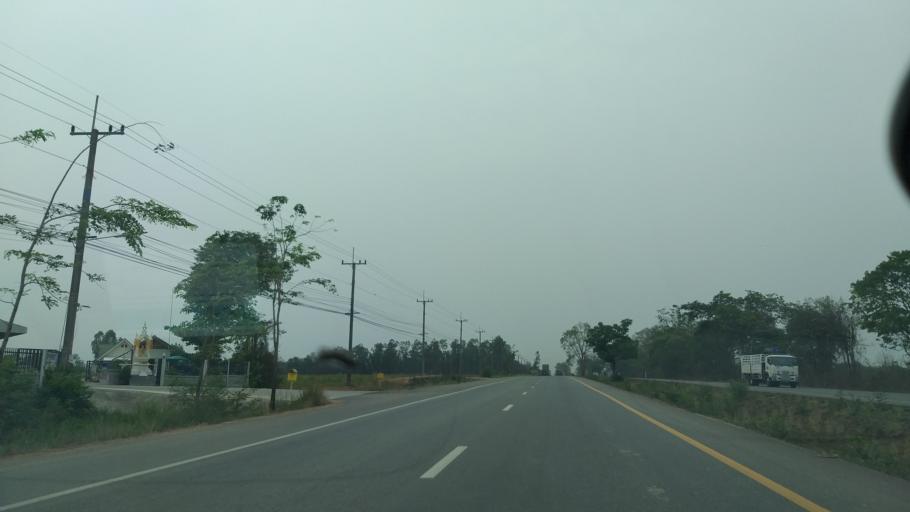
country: TH
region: Chachoengsao
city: Plaeng Yao
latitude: 13.5046
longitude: 101.2702
